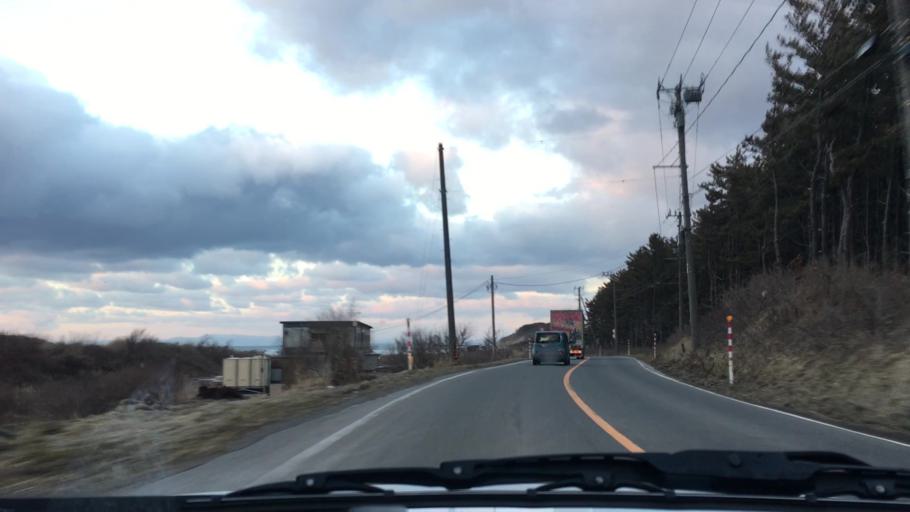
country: JP
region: Aomori
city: Shimokizukuri
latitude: 40.7522
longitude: 140.1466
